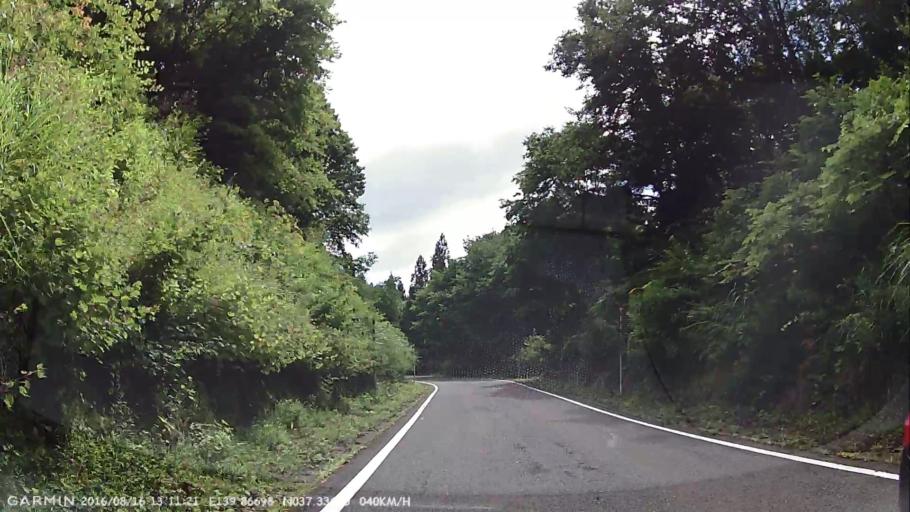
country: JP
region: Fukushima
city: Kitakata
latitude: 37.3366
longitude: 139.8670
